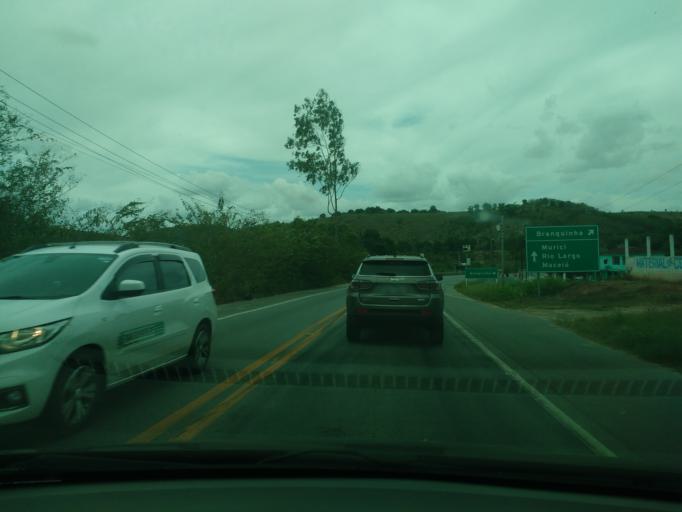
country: BR
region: Alagoas
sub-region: Uniao Dos Palmares
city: Uniao dos Palmares
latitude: -9.2411
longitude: -36.0132
